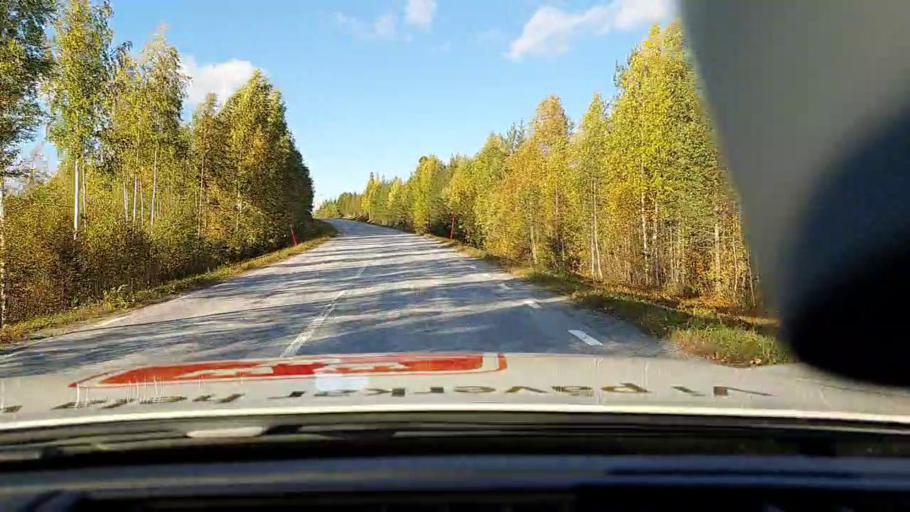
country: SE
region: Norrbotten
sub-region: Pitea Kommun
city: Norrfjarden
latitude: 65.4504
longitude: 21.4568
